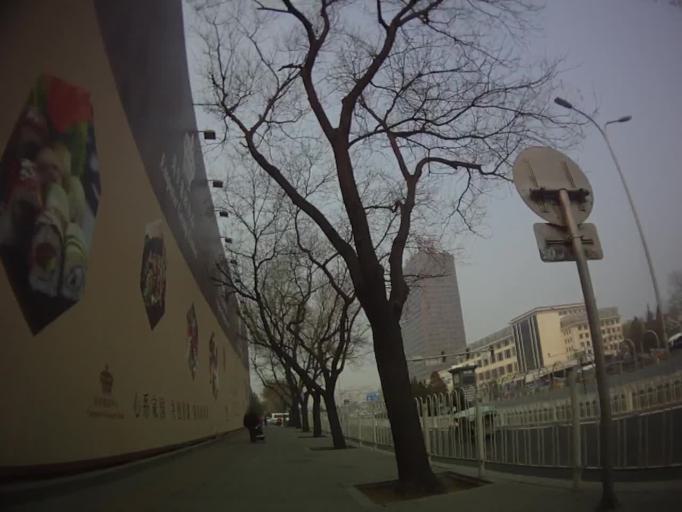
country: CN
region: Beijing
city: Chaowai
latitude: 39.9068
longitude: 116.4385
